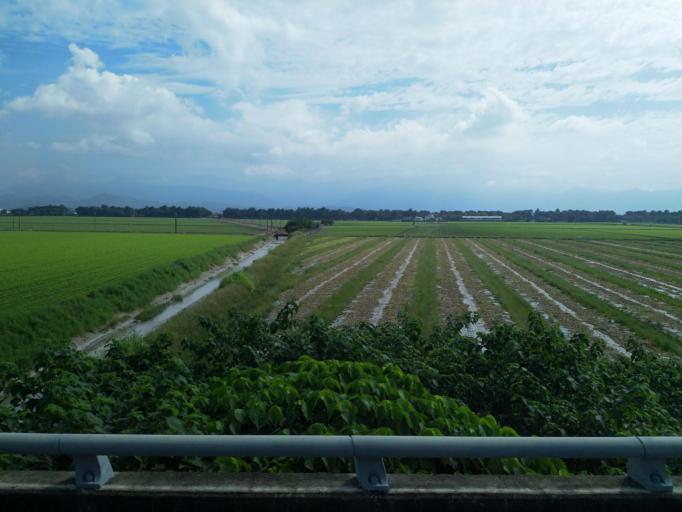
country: TW
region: Taiwan
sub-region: Pingtung
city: Pingtung
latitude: 22.8486
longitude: 120.4948
